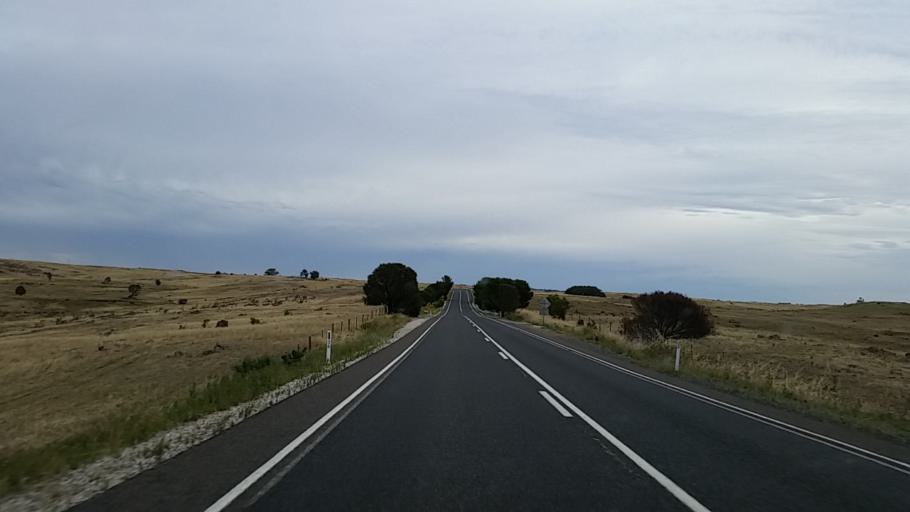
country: AU
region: South Australia
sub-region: Mid Murray
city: Mannum
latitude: -34.7569
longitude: 139.1778
